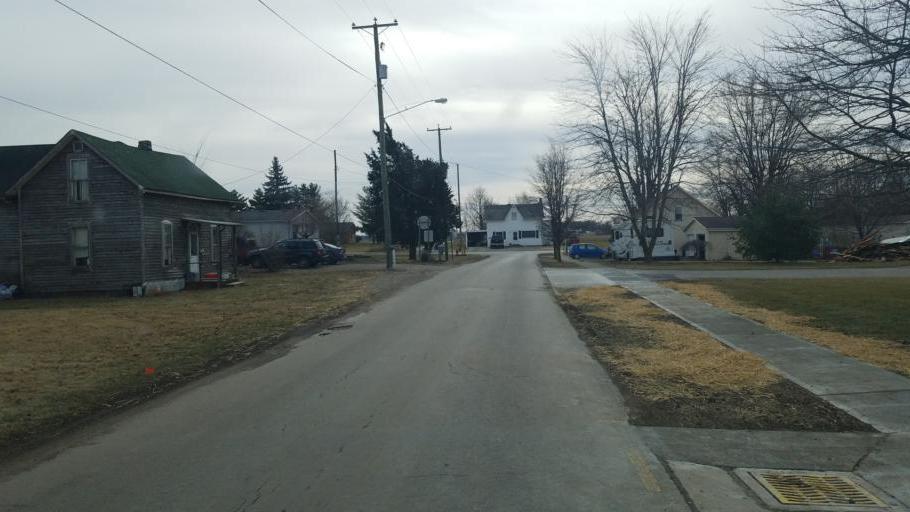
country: US
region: Ohio
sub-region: Hardin County
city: Kenton
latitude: 40.5345
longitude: -83.5154
